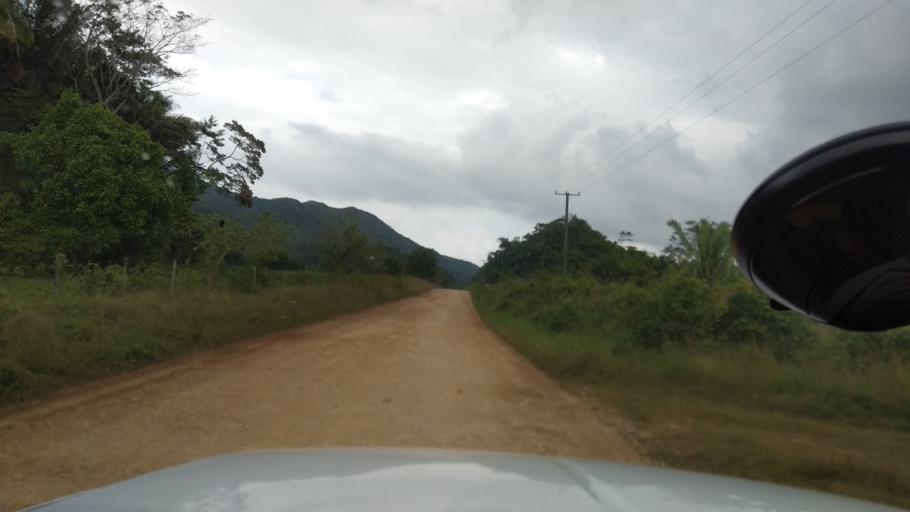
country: BZ
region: Toledo
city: Punta Gorda
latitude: 16.2039
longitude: -89.0326
